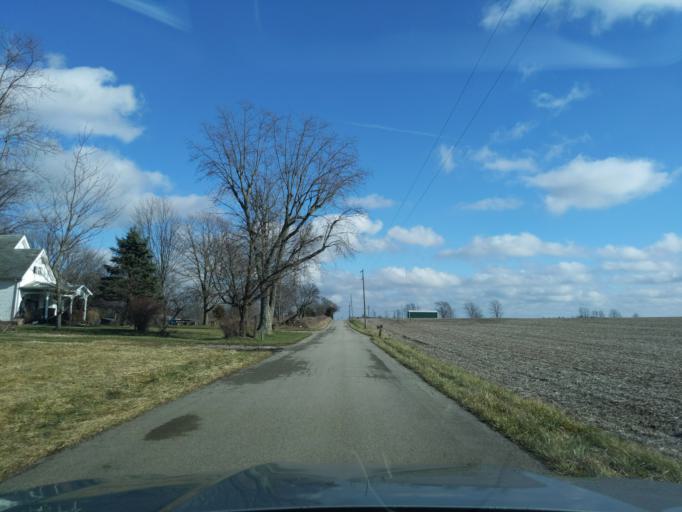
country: US
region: Indiana
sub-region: Decatur County
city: Greensburg
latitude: 39.2781
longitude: -85.4735
